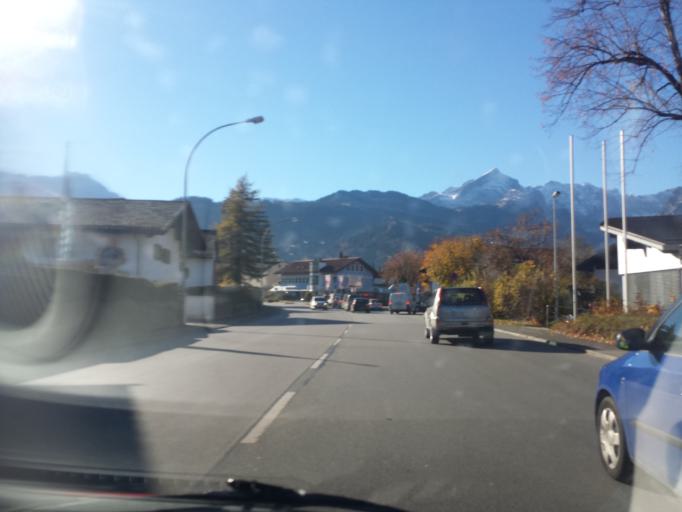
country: DE
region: Bavaria
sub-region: Upper Bavaria
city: Garmisch-Partenkirchen
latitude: 47.4999
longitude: 11.1014
